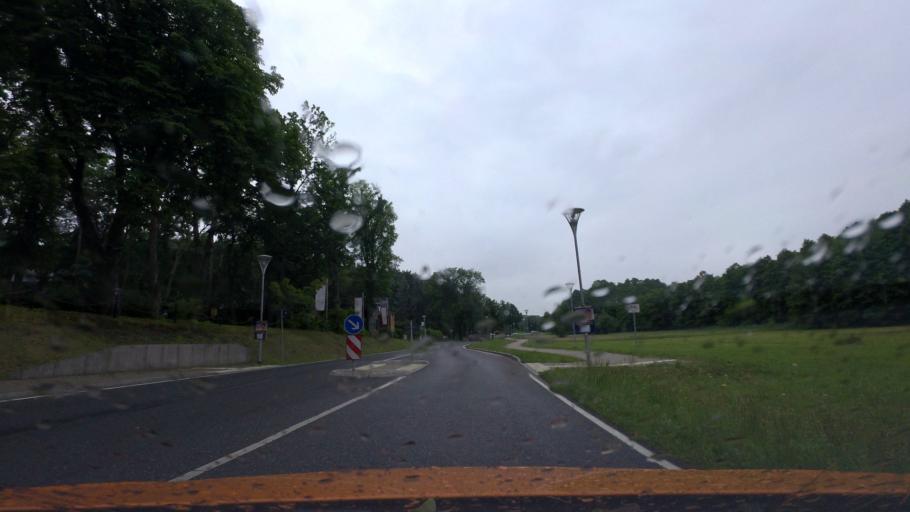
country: DE
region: Brandenburg
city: Strausberg
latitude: 52.5956
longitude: 13.8918
